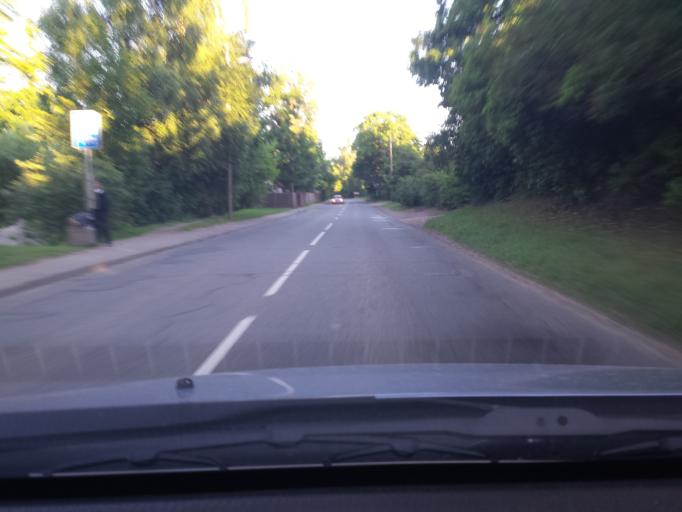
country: LV
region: Riga
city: Jaunciems
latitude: 57.0396
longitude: 24.1750
